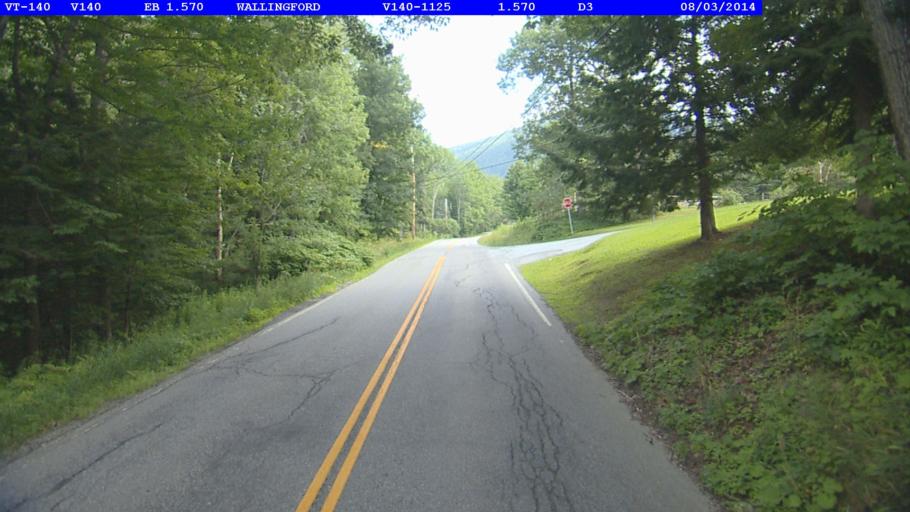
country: US
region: Vermont
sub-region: Rutland County
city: Rutland
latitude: 43.4614
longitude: -72.9515
